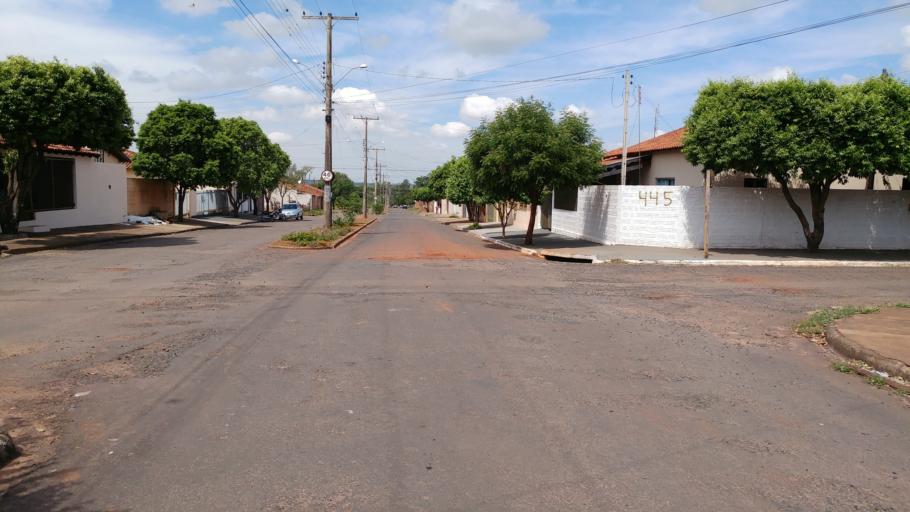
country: BR
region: Sao Paulo
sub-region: Paraguacu Paulista
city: Paraguacu Paulista
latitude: -22.4321
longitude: -50.5766
